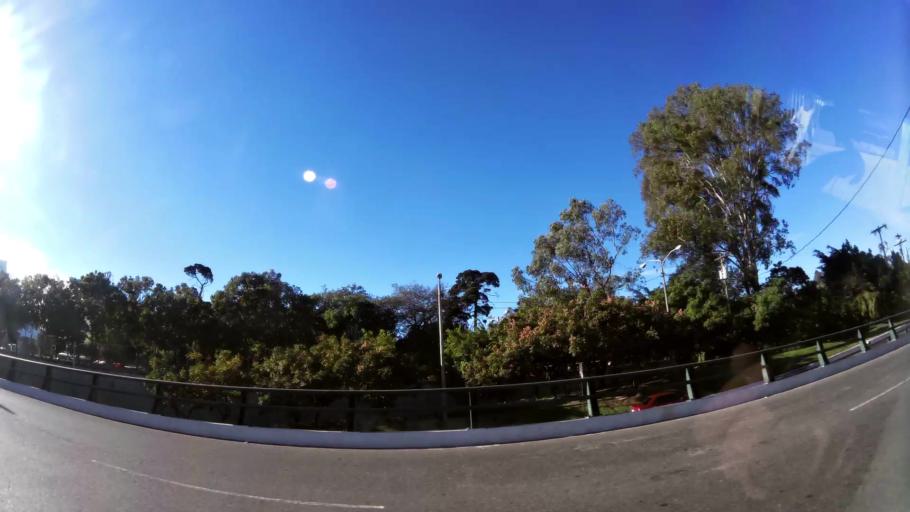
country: GT
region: Guatemala
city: Santa Catarina Pinula
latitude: 14.5953
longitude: -90.5192
